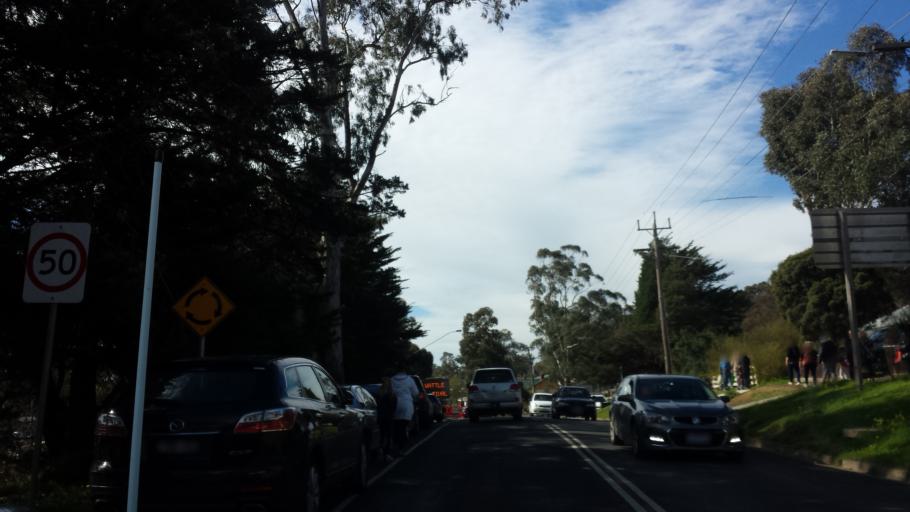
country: AU
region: Victoria
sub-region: Nillumbik
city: Hurstbridge
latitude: -37.6410
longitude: 145.1916
